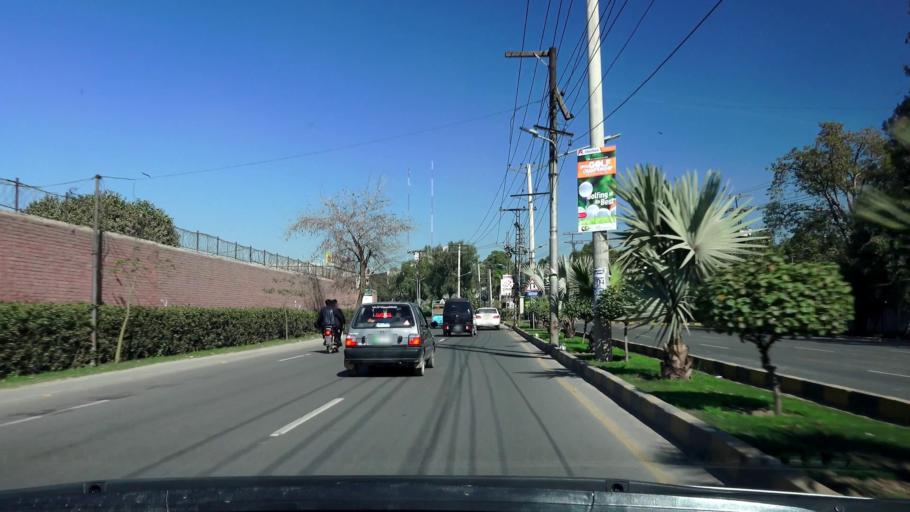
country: PK
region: Punjab
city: Faisalabad
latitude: 31.4314
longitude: 73.0779
